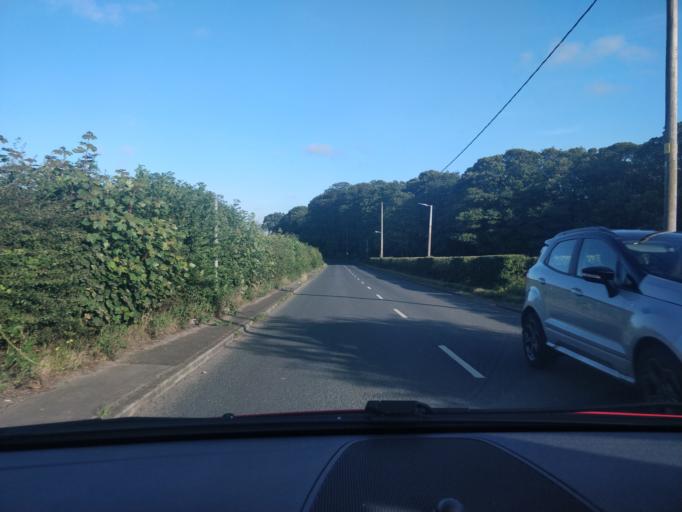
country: GB
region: England
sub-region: Lancashire
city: Tarleton
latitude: 53.6495
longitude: -2.8736
